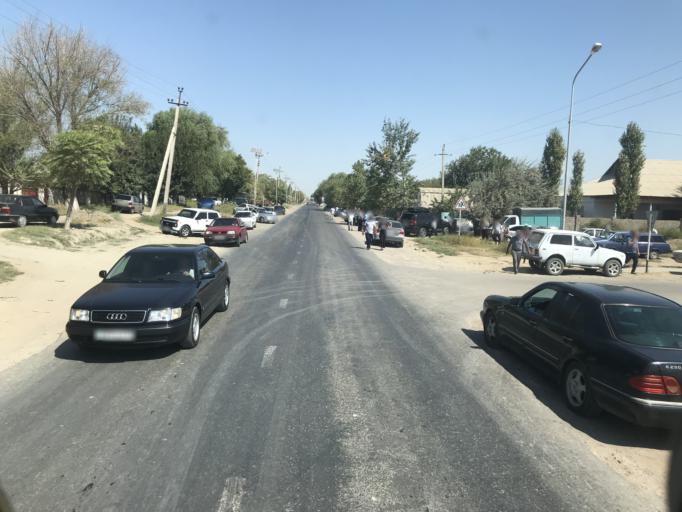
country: KZ
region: Ongtustik Qazaqstan
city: Ilyich
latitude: 40.9326
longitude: 68.4883
